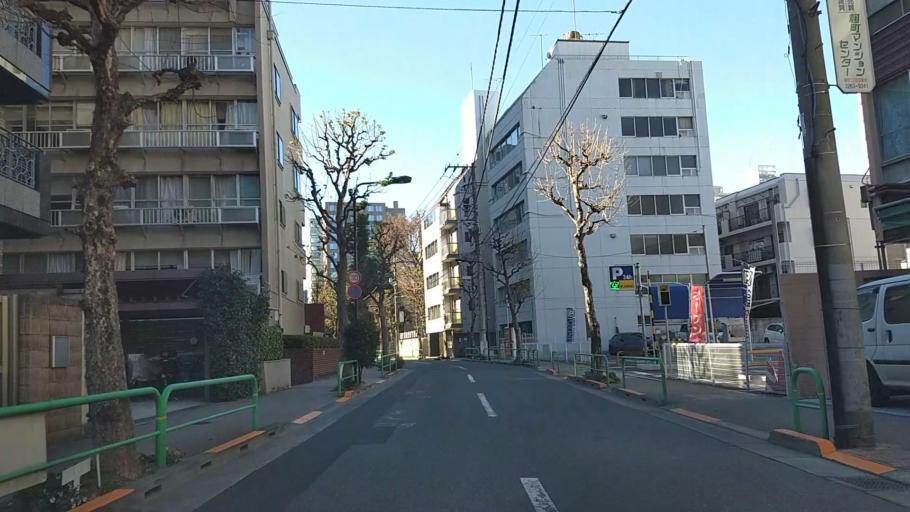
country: JP
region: Tokyo
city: Tokyo
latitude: 35.6904
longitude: 139.7421
